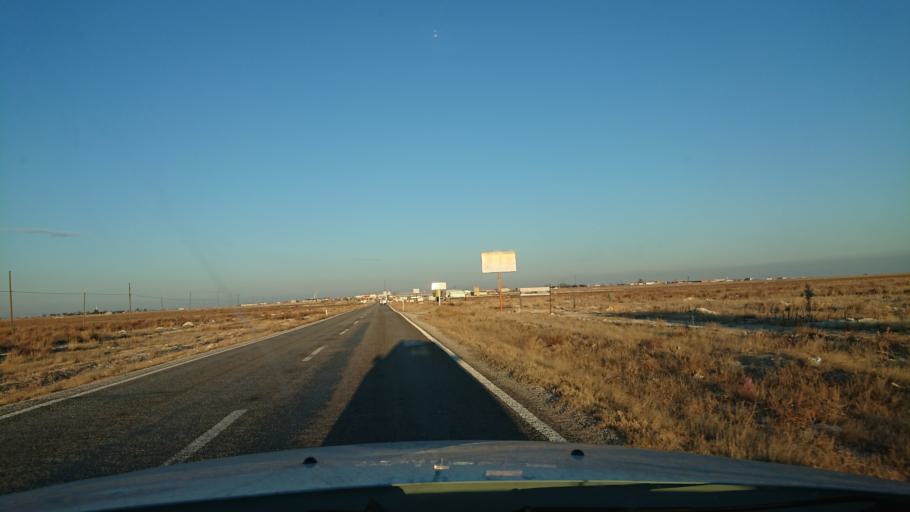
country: TR
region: Aksaray
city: Eskil
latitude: 38.3887
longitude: 33.3848
